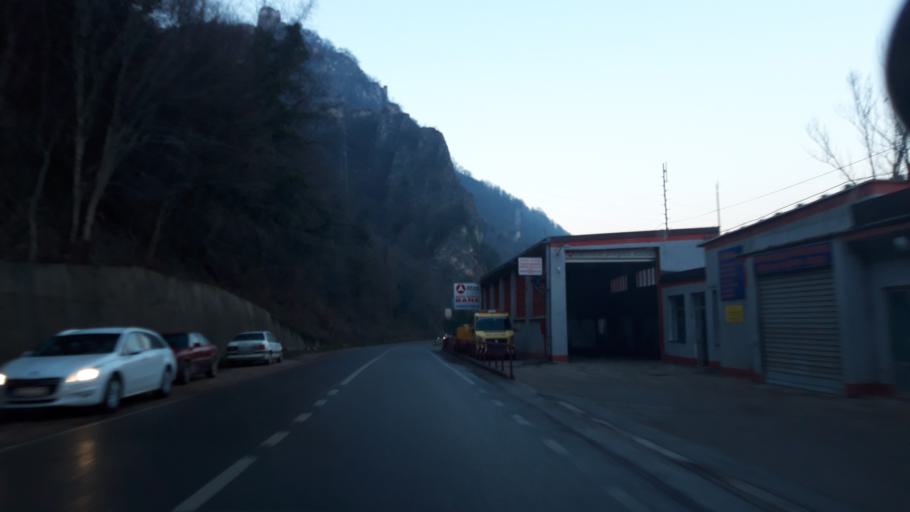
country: RS
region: Central Serbia
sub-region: Macvanski Okrug
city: Mali Zvornik
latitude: 44.3706
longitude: 19.1019
